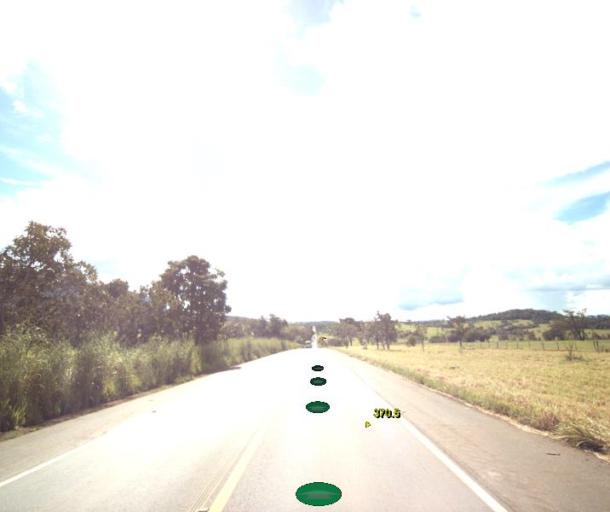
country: BR
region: Goias
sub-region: Jaragua
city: Jaragua
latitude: -15.8263
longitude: -49.2822
